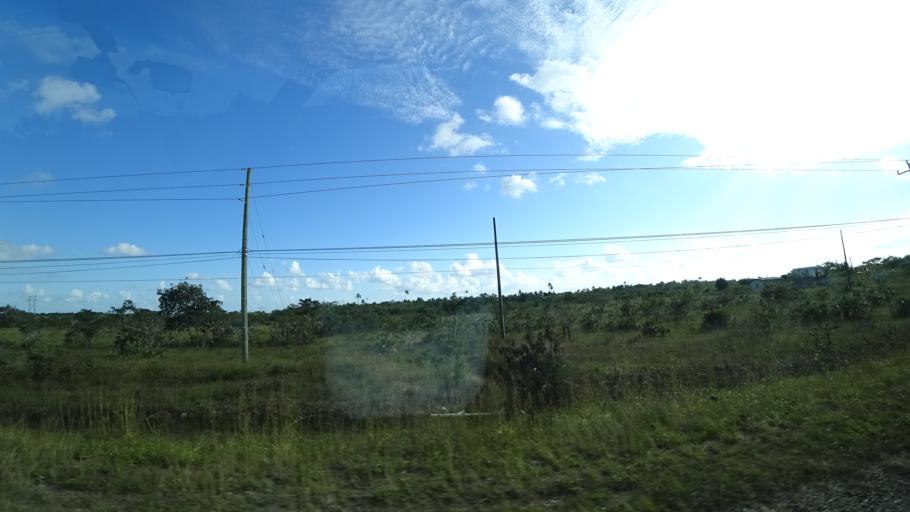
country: BZ
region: Belize
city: Belize City
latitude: 17.5815
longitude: -88.3645
